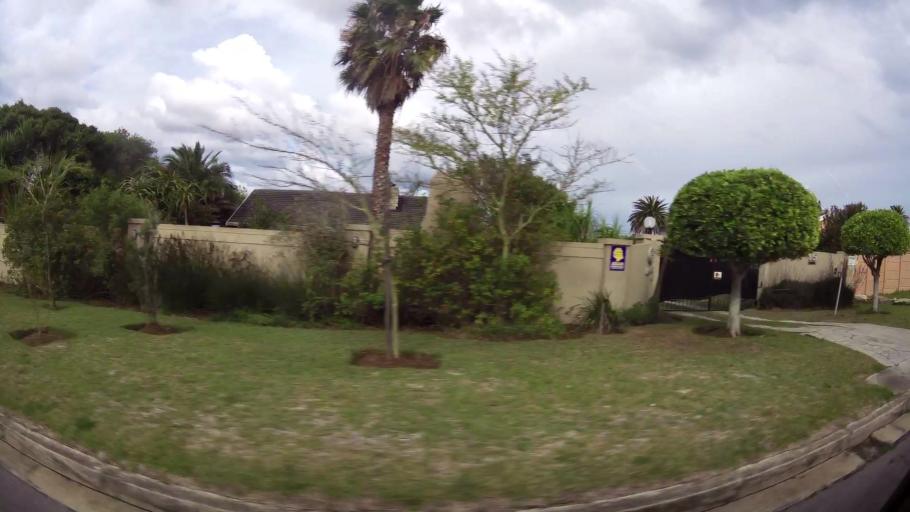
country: ZA
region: Eastern Cape
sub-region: Nelson Mandela Bay Metropolitan Municipality
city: Port Elizabeth
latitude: -33.9366
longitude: 25.5103
